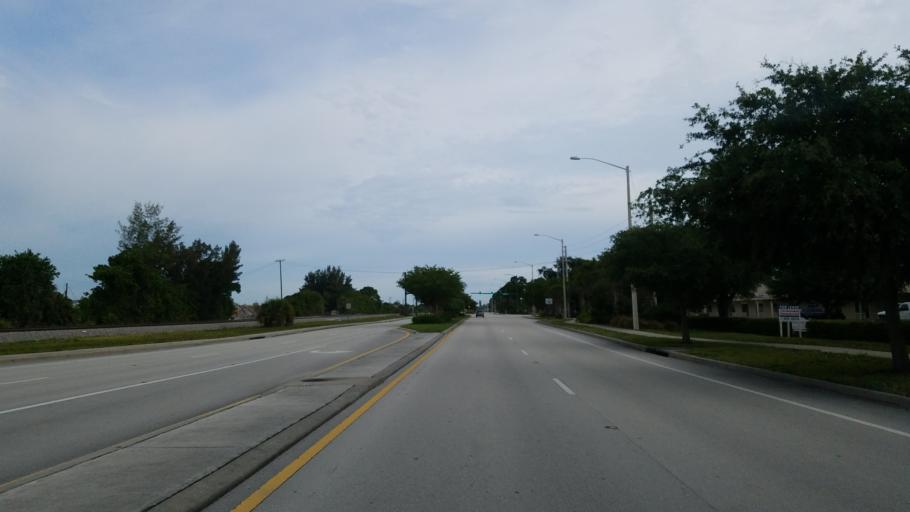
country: US
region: Florida
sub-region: Martin County
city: Stuart
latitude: 27.1745
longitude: -80.2295
